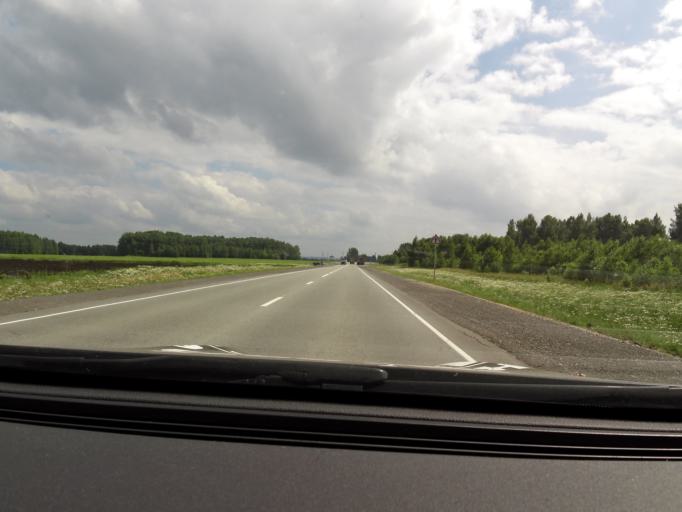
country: RU
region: Perm
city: Suksun
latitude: 56.9814
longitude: 57.5086
